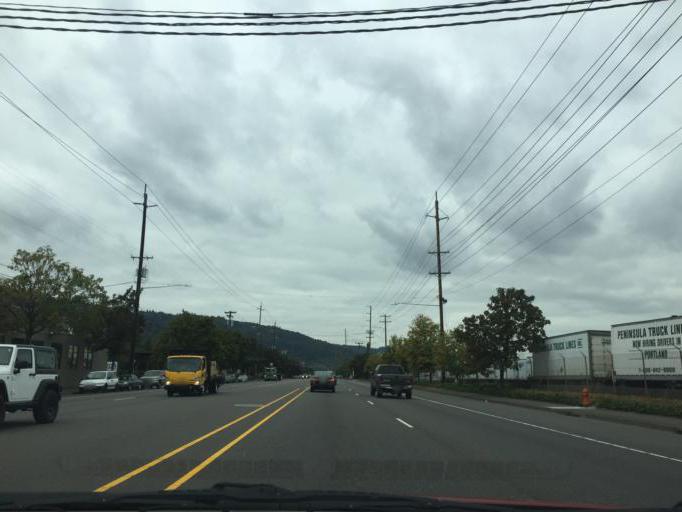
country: US
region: Oregon
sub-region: Multnomah County
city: Portland
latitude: 45.5444
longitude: -122.7037
